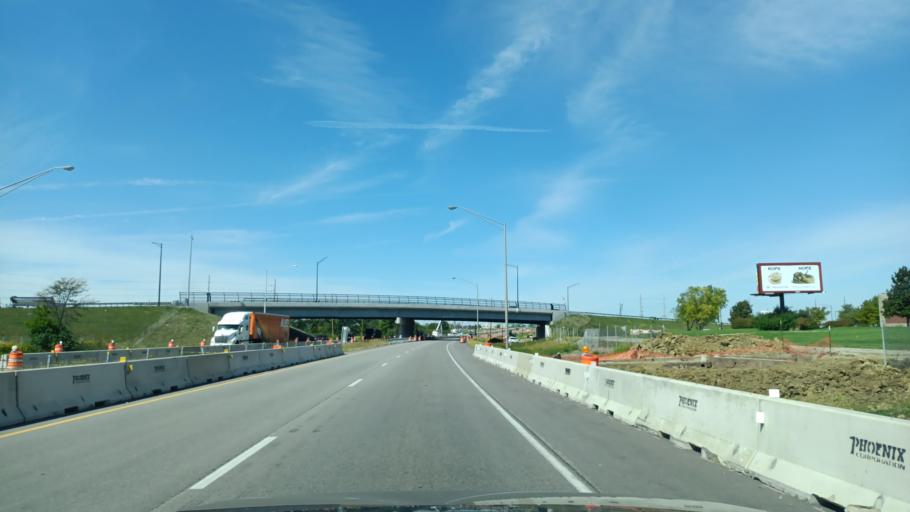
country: US
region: Illinois
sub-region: Champaign County
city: Champaign
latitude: 40.1403
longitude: -88.2750
